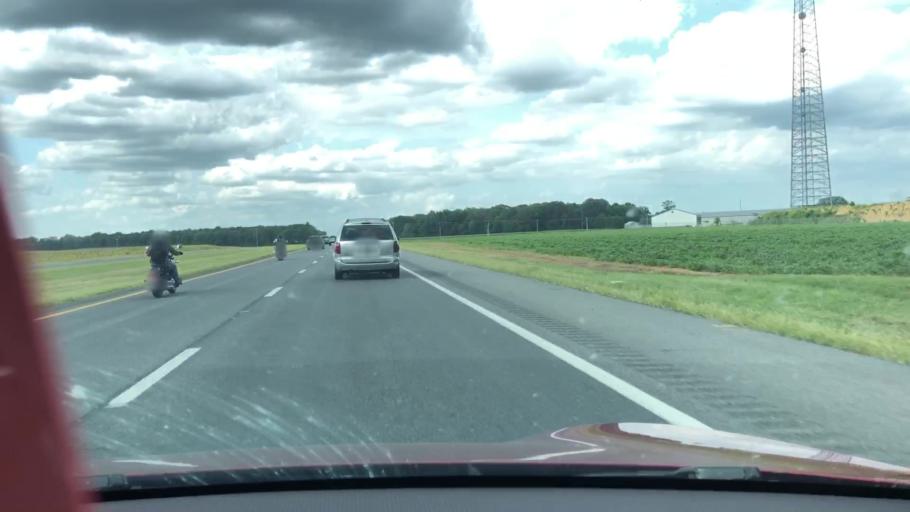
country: US
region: Delaware
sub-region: Sussex County
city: Laurel
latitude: 38.5087
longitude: -75.5567
